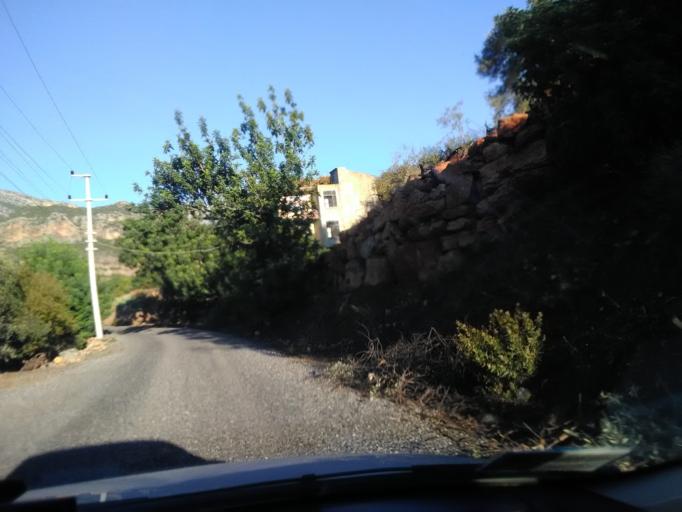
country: TR
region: Antalya
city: Gazipasa
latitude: 36.3182
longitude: 32.4190
